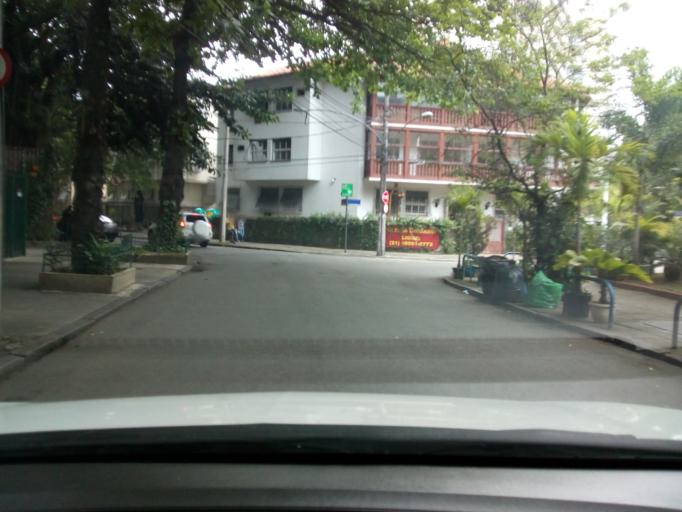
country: BR
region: Rio de Janeiro
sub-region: Rio De Janeiro
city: Rio de Janeiro
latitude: -22.9815
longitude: -43.2262
